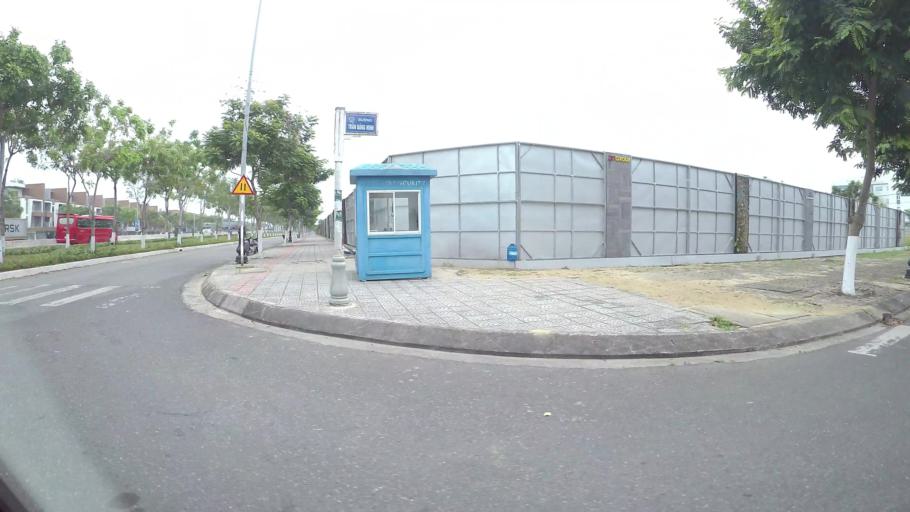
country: VN
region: Da Nang
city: Son Tra
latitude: 16.0337
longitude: 108.2290
